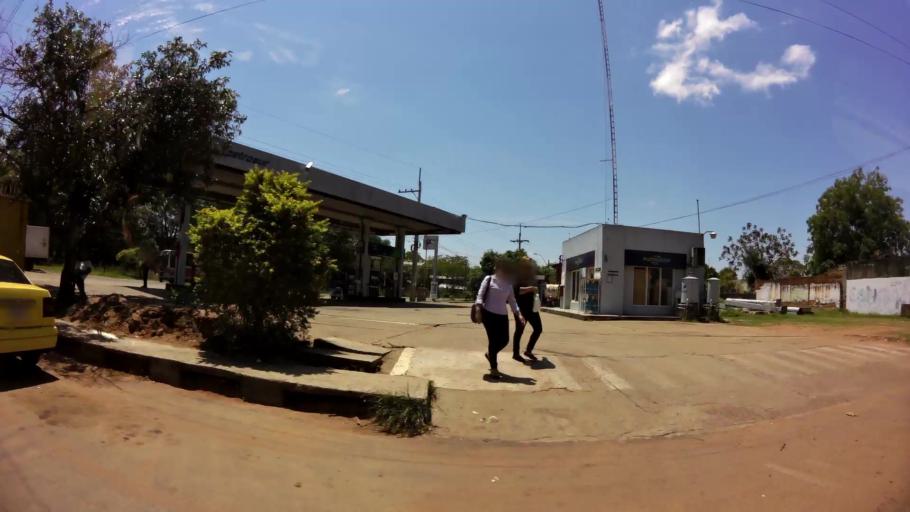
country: PY
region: Central
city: Nemby
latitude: -25.3985
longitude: -57.5344
